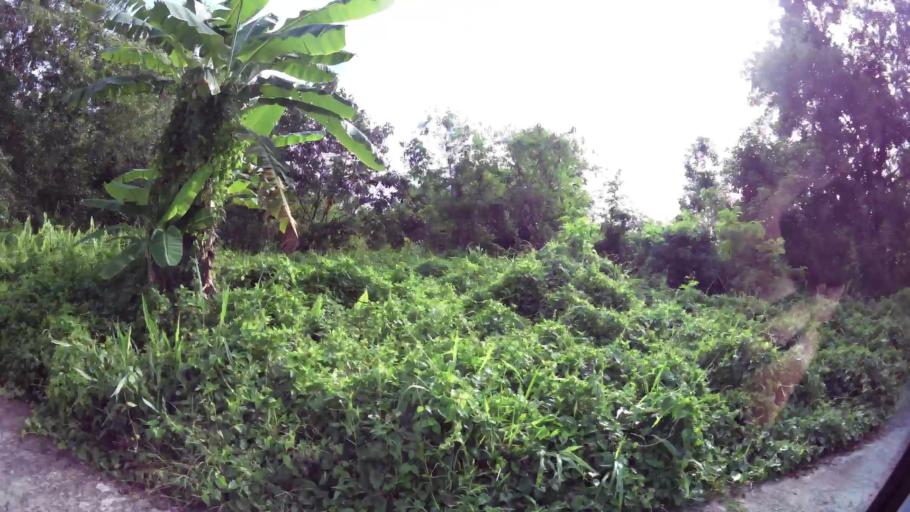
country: BN
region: Brunei and Muara
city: Bandar Seri Begawan
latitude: 4.8924
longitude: 114.9676
